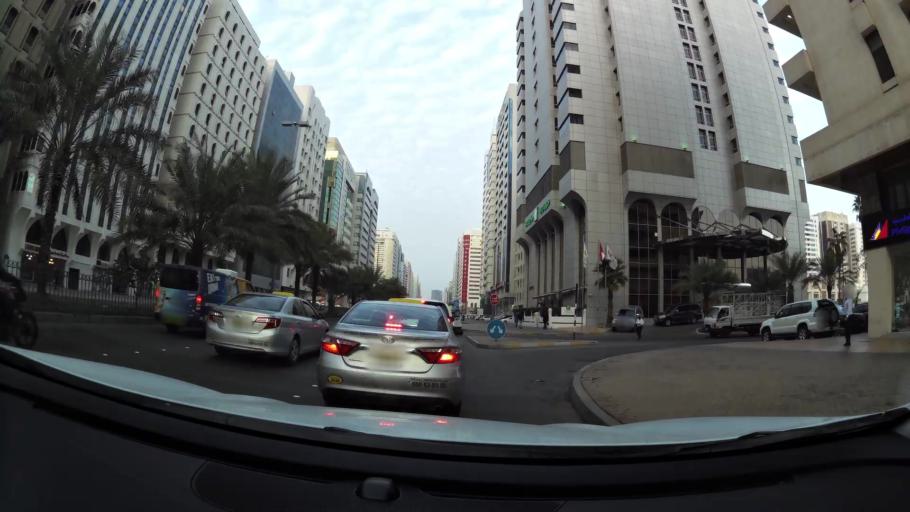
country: AE
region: Abu Dhabi
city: Abu Dhabi
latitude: 24.4890
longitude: 54.3676
